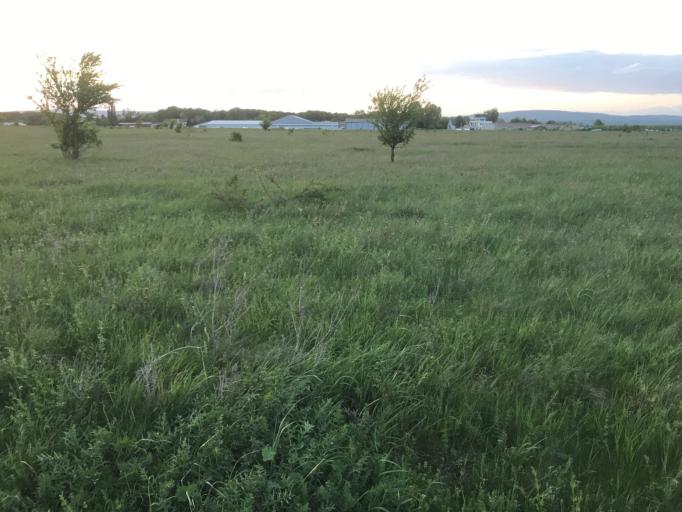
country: DE
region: Rheinland-Pfalz
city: Wackernheim
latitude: 49.9680
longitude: 8.1533
